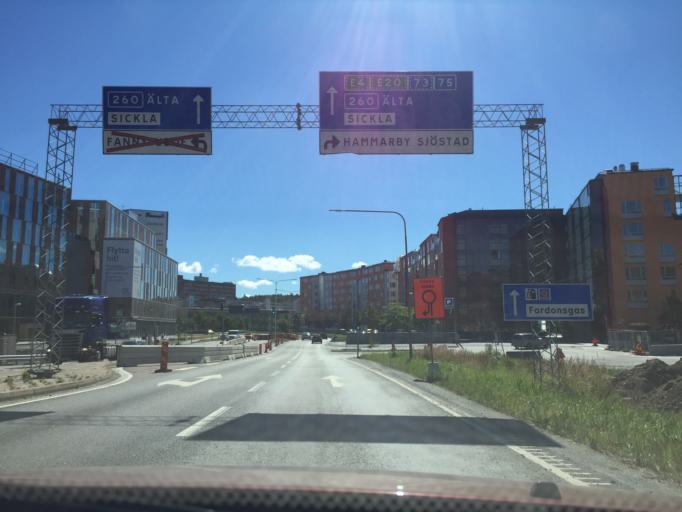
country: SE
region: Stockholm
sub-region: Stockholms Kommun
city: OEstermalm
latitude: 59.3065
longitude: 18.1132
